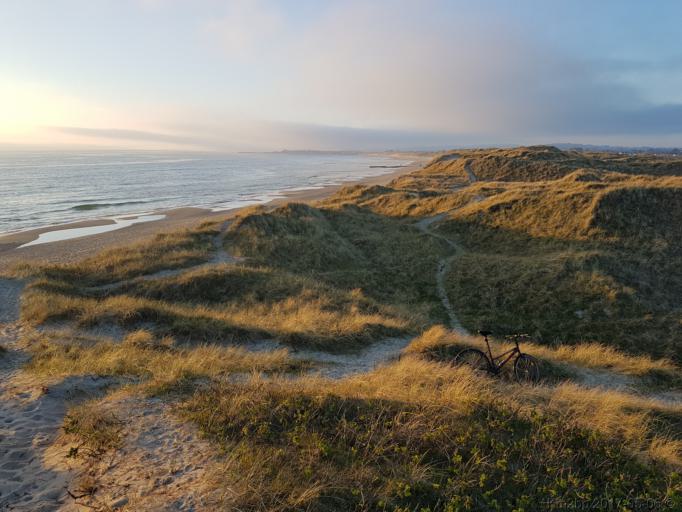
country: NO
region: Rogaland
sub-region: Klepp
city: Kleppe
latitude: 58.7911
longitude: 5.5458
